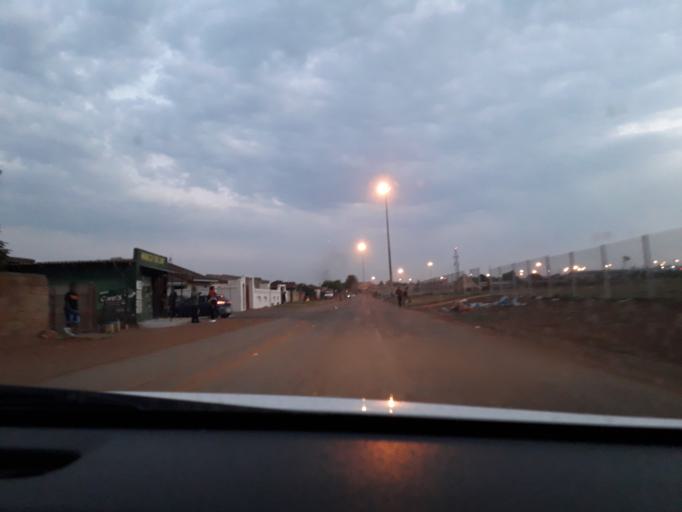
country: ZA
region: Gauteng
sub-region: Ekurhuleni Metropolitan Municipality
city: Tembisa
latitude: -25.9985
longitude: 28.2380
